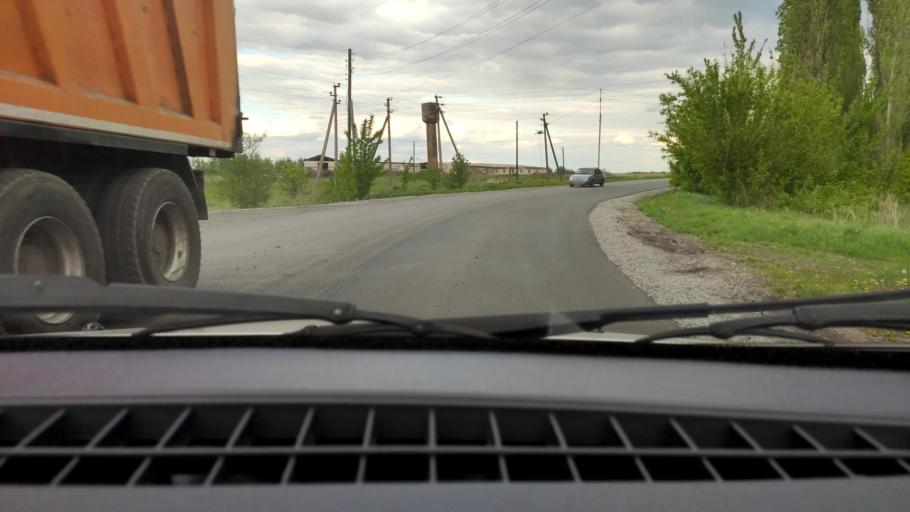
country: RU
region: Voronezj
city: Podkletnoye
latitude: 51.5907
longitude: 39.4703
